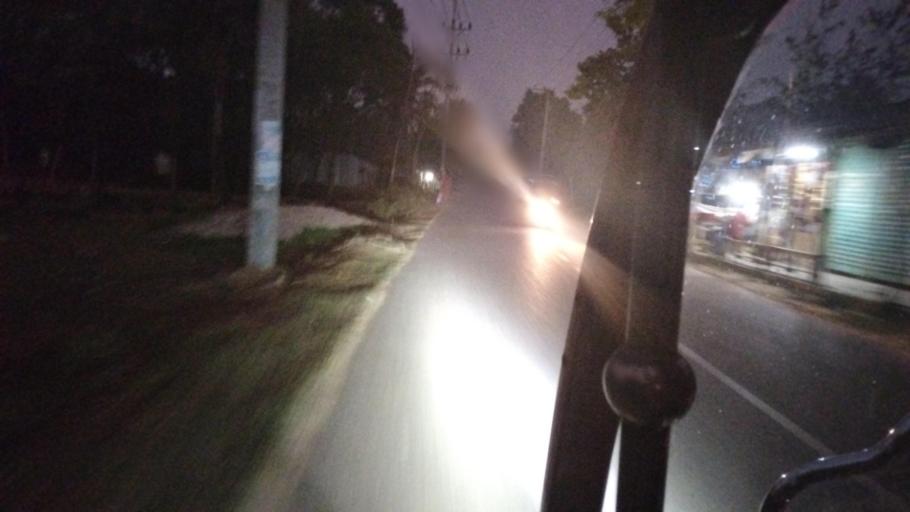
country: BD
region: Dhaka
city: Sakhipur
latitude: 24.4005
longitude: 90.3495
